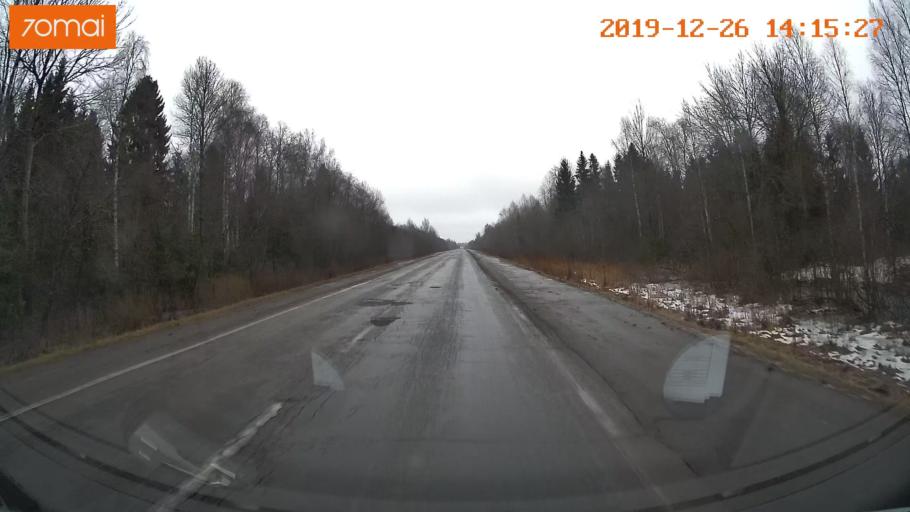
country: RU
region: Jaroslavl
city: Poshekhon'ye
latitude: 58.5155
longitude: 39.0454
